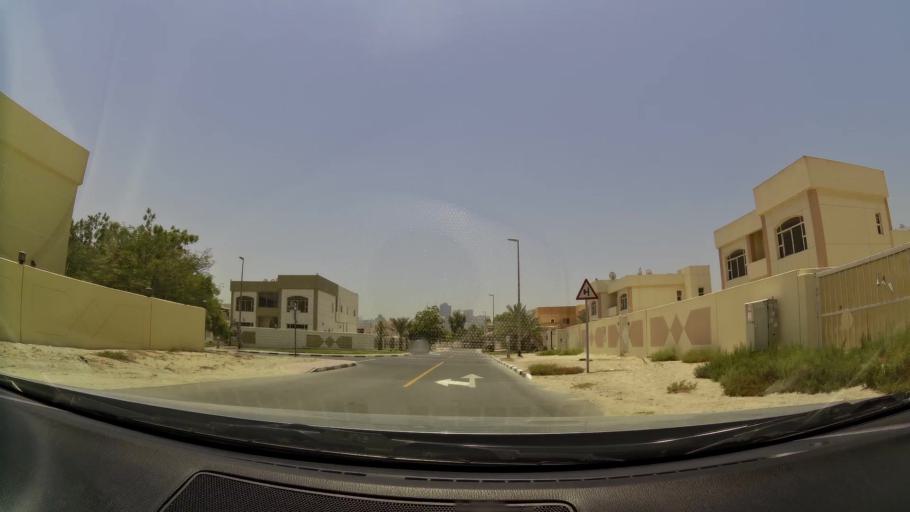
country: AE
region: Dubai
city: Dubai
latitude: 25.1038
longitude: 55.1948
